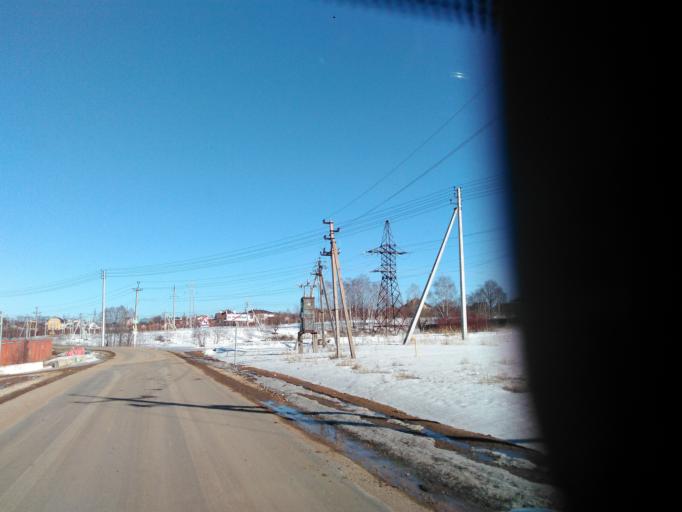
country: RU
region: Moskovskaya
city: Yermolino
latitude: 56.1510
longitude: 37.4724
